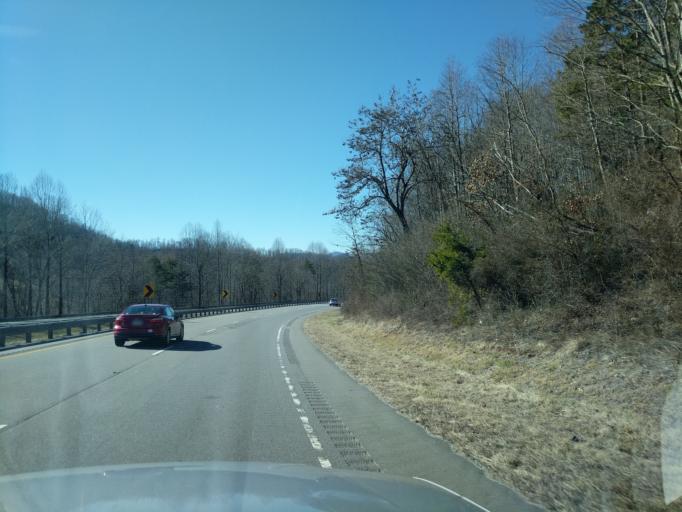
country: US
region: North Carolina
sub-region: Jackson County
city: Sylva
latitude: 35.3938
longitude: -83.1592
